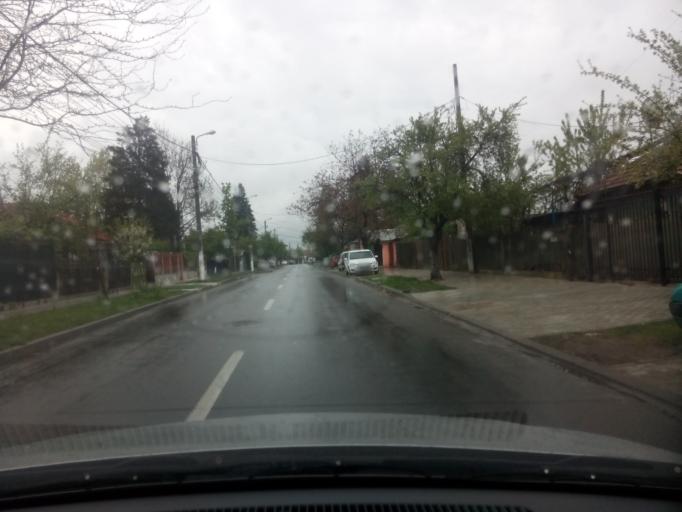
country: RO
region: Ilfov
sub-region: Voluntari City
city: Voluntari
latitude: 44.4856
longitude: 26.1662
